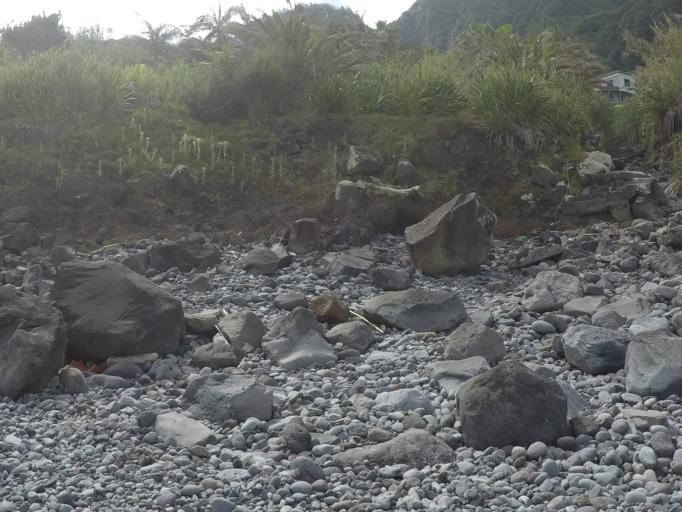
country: PT
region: Madeira
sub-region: Sao Vicente
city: Sao Vicente
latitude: 32.8247
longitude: -16.9987
